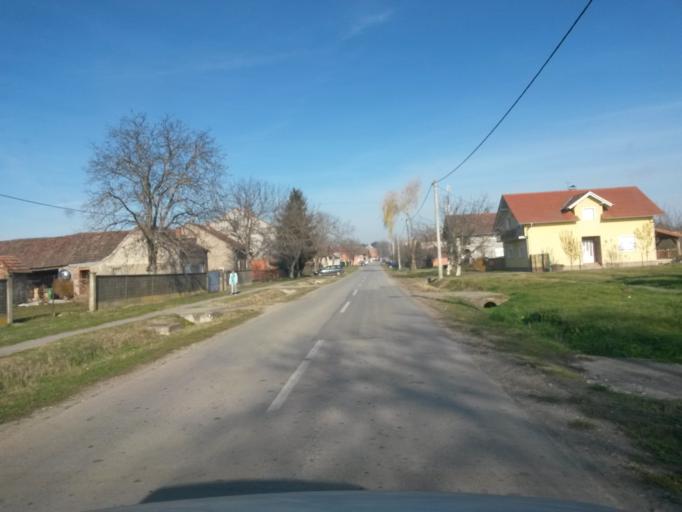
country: HR
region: Vukovarsko-Srijemska
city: Slakovci
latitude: 45.2490
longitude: 18.9040
